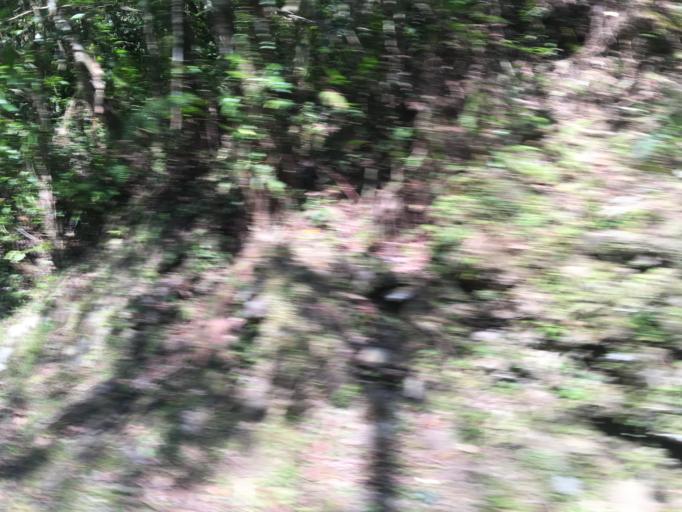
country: TW
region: Taiwan
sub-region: Yilan
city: Yilan
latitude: 24.7568
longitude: 121.6220
